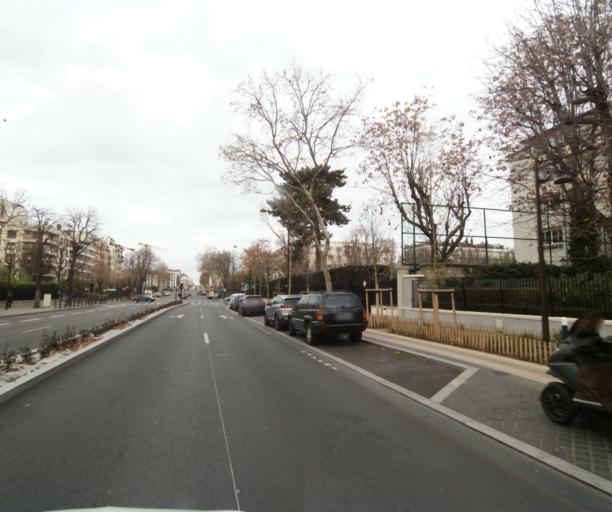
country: FR
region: Ile-de-France
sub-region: Departement des Hauts-de-Seine
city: Neuilly-sur-Seine
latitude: 48.8918
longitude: 2.2694
